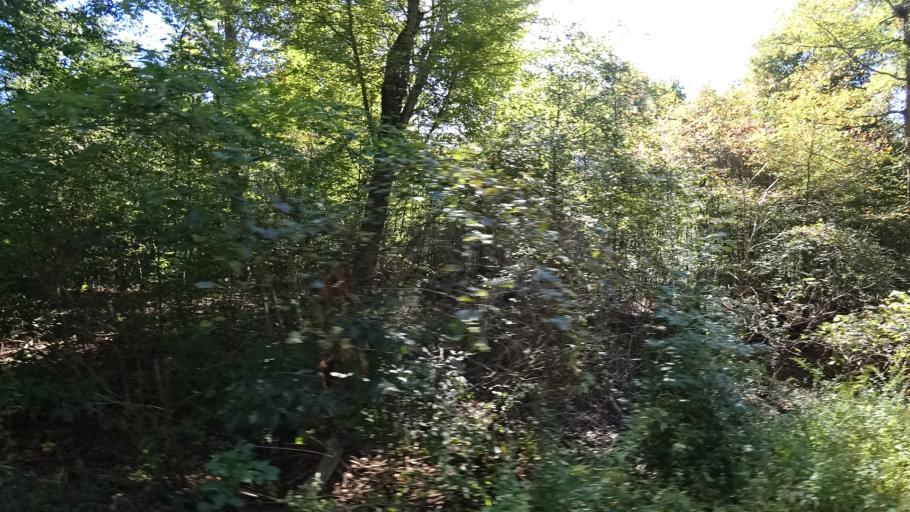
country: US
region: Indiana
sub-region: LaPorte County
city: Long Beach
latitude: 41.7454
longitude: -86.8192
